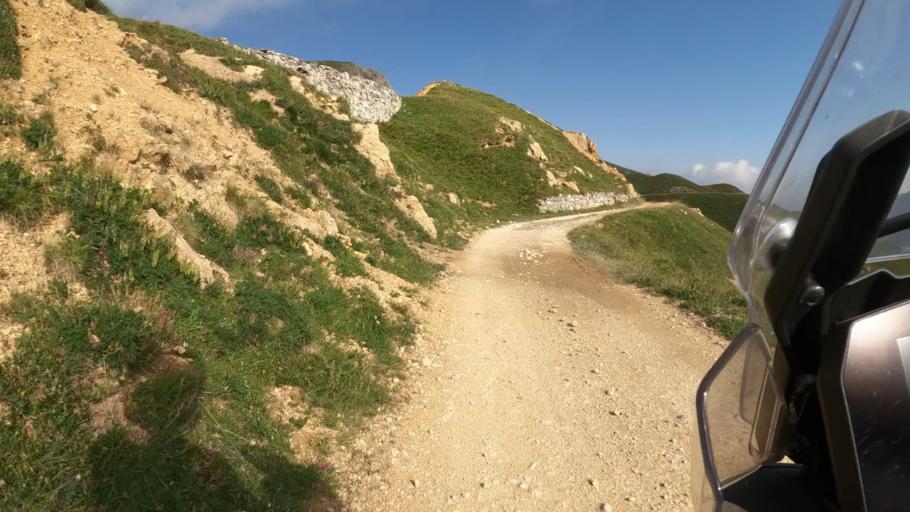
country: IT
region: Piedmont
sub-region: Provincia di Cuneo
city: Pietraporzio
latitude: 44.3809
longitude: 7.0543
